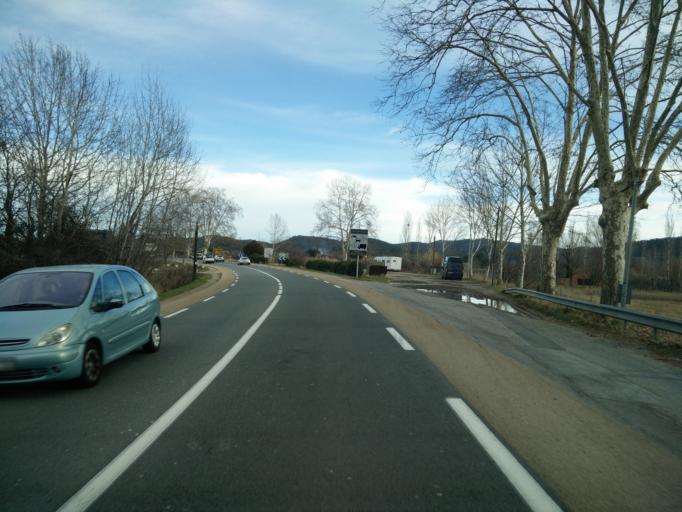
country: FR
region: Provence-Alpes-Cote d'Azur
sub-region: Departement du Var
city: Les Arcs
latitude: 43.4471
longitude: 6.4816
